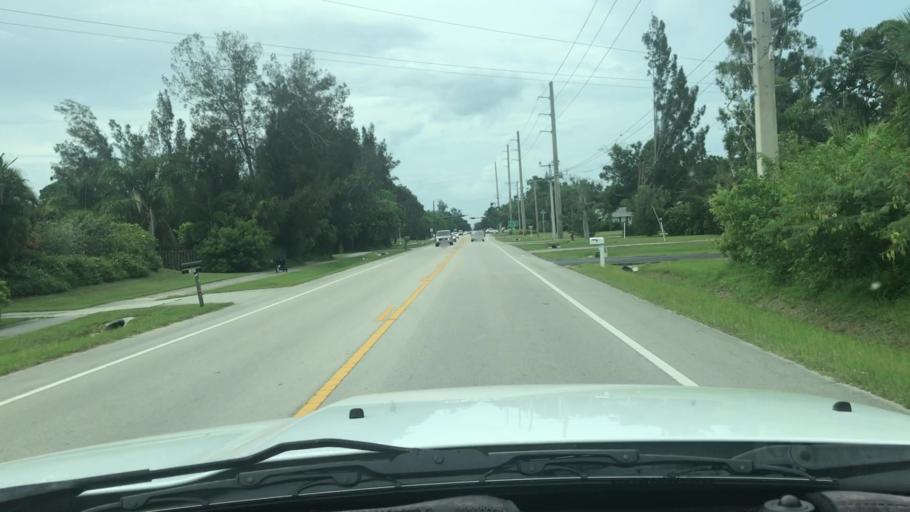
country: US
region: Florida
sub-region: Indian River County
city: Vero Beach South
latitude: 27.6210
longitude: -80.4139
